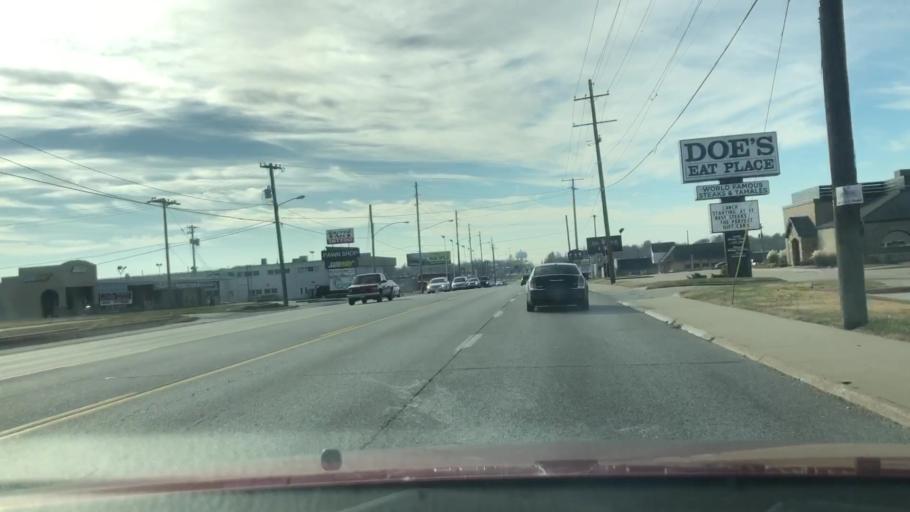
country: US
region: Missouri
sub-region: Greene County
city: Springfield
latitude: 37.2182
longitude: -93.2617
